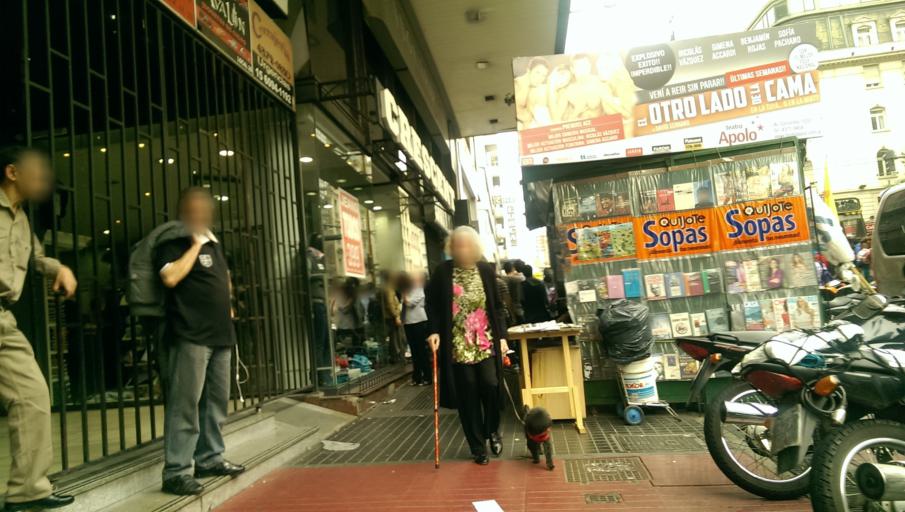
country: AR
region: Buenos Aires F.D.
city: Buenos Aires
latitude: -34.6040
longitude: -58.3860
